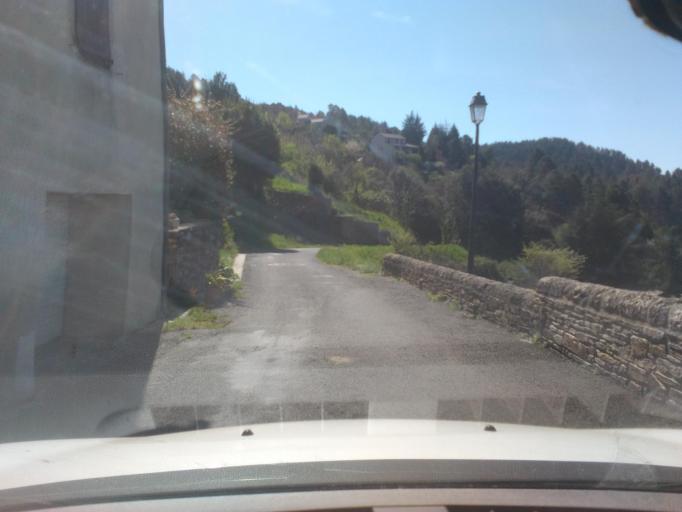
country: FR
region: Languedoc-Roussillon
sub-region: Departement du Gard
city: Saint-Jean-du-Gard
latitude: 44.1471
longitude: 3.7727
